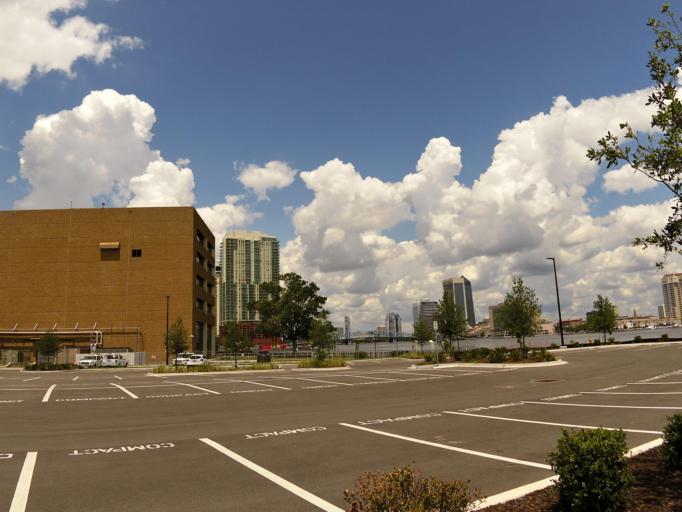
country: US
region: Florida
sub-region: Duval County
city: Jacksonville
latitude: 30.3172
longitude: -81.6493
